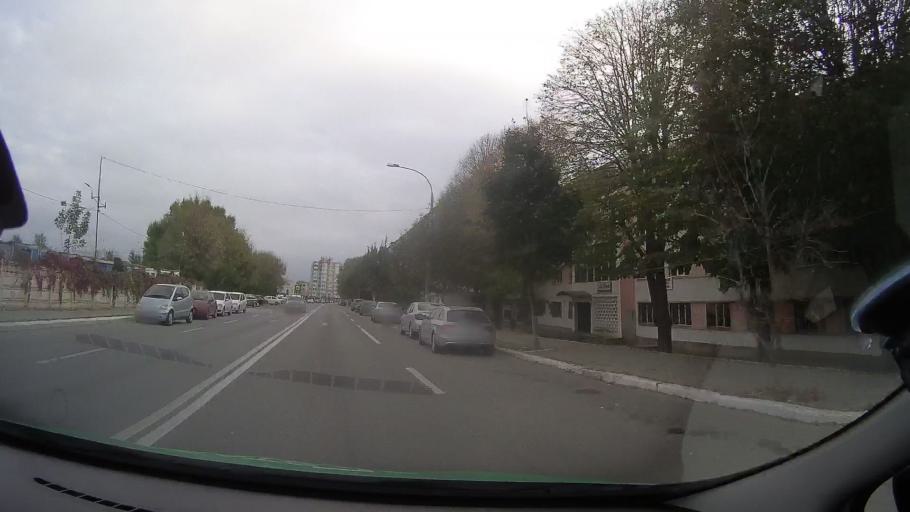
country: RO
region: Constanta
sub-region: Municipiul Medgidia
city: Medgidia
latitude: 44.2639
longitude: 28.2602
